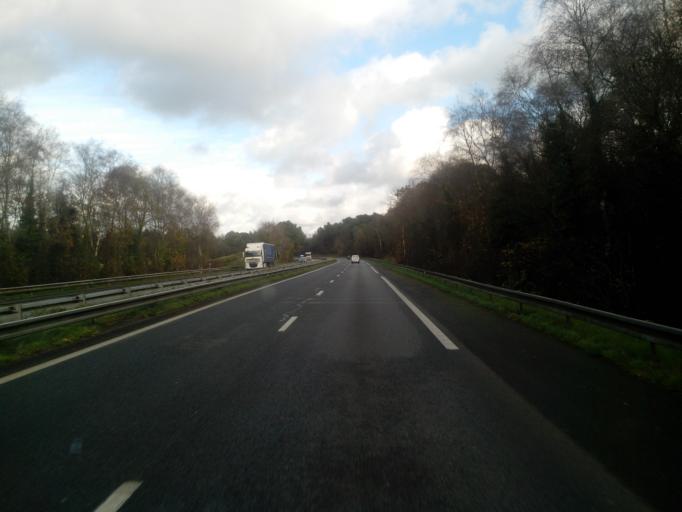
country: FR
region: Brittany
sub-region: Departement du Morbihan
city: Languidic
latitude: 47.8422
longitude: -3.1358
